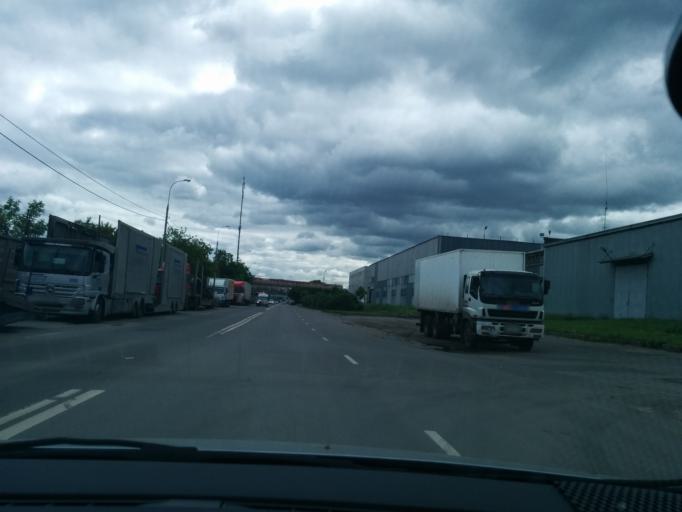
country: RU
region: Moscow
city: Tekstil'shchiki
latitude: 55.7078
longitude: 37.7114
